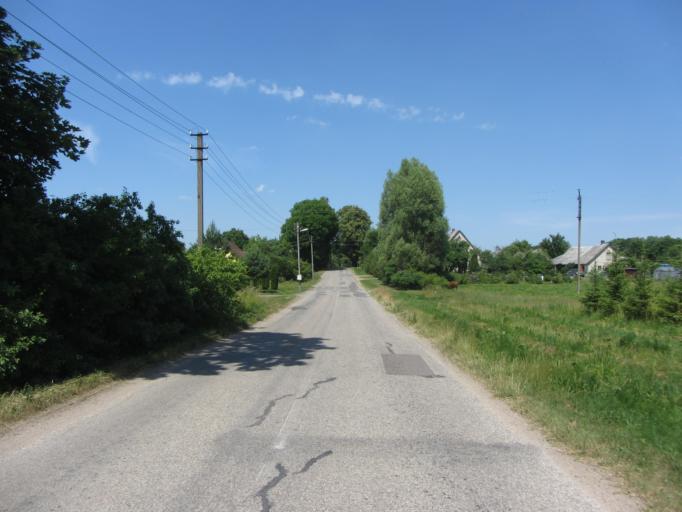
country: LT
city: Sirvintos
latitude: 55.1738
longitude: 24.9706
